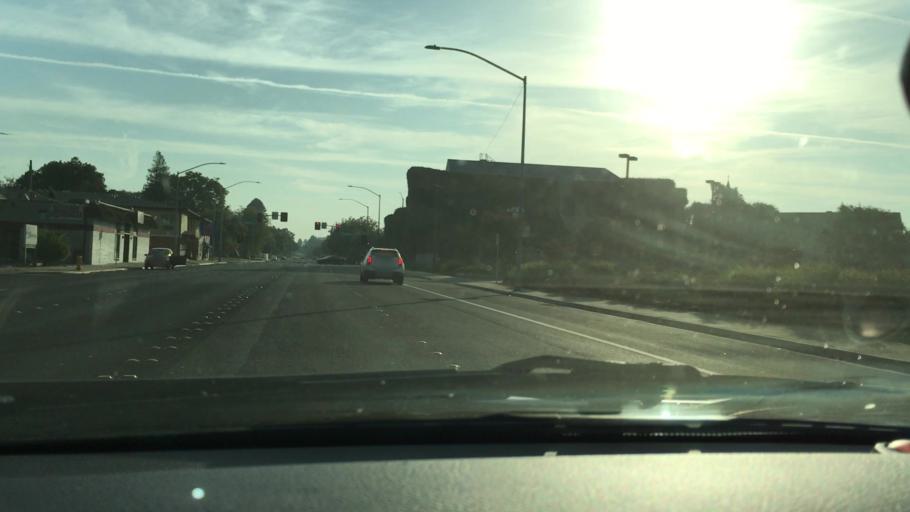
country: US
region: California
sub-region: Stanislaus County
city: Modesto
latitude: 37.6458
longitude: -121.0044
